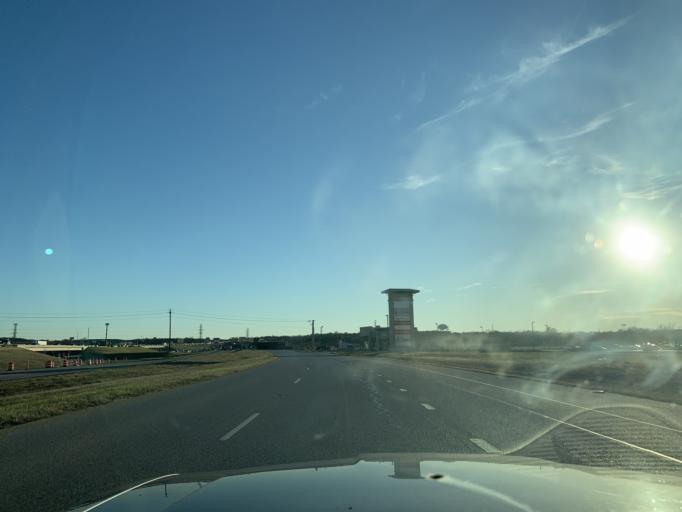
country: US
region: Texas
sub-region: Tarrant County
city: Euless
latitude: 32.8721
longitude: -97.1012
